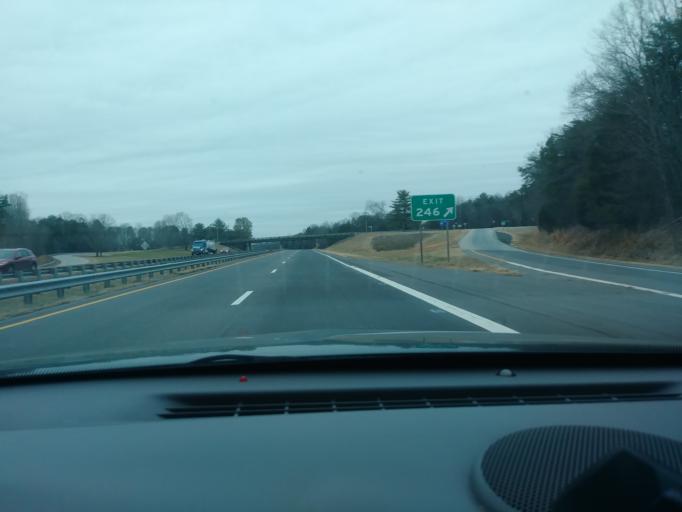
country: US
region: North Carolina
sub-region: Forsyth County
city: Lewisville
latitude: 36.1002
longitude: -80.4659
